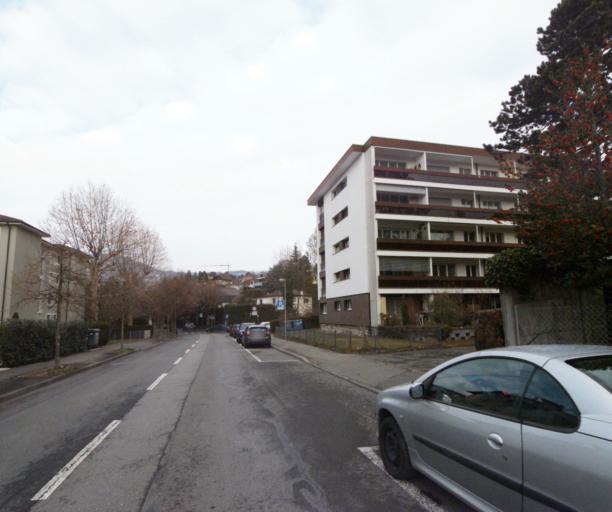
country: CH
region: Vaud
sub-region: Riviera-Pays-d'Enhaut District
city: La Tour-de-Peilz
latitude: 46.4593
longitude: 6.8614
